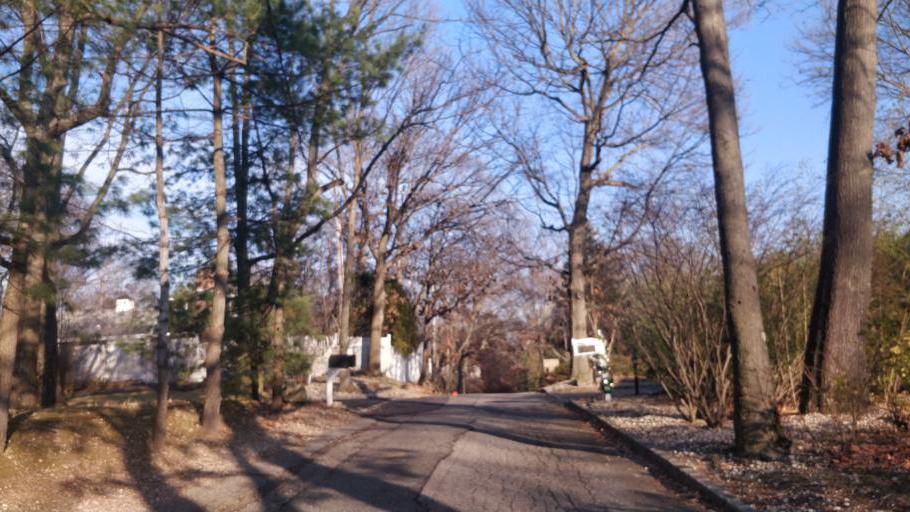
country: US
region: New York
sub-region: Nassau County
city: Bayville
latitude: 40.9010
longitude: -73.5670
